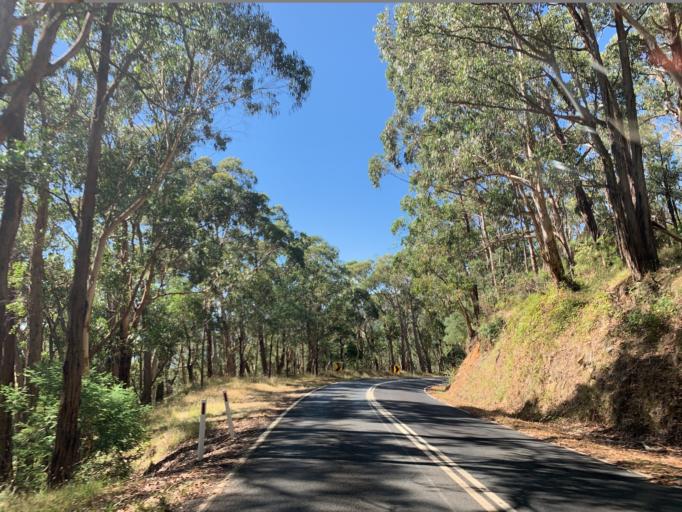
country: AU
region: Victoria
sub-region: Yarra Ranges
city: Badger Creek
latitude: -37.6972
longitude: 145.5591
